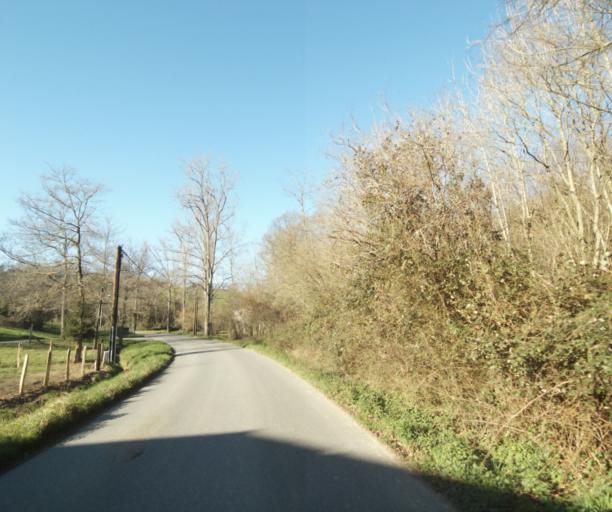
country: FR
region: Aquitaine
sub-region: Departement des Pyrenees-Atlantiques
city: Hendaye
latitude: 43.3591
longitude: -1.7531
